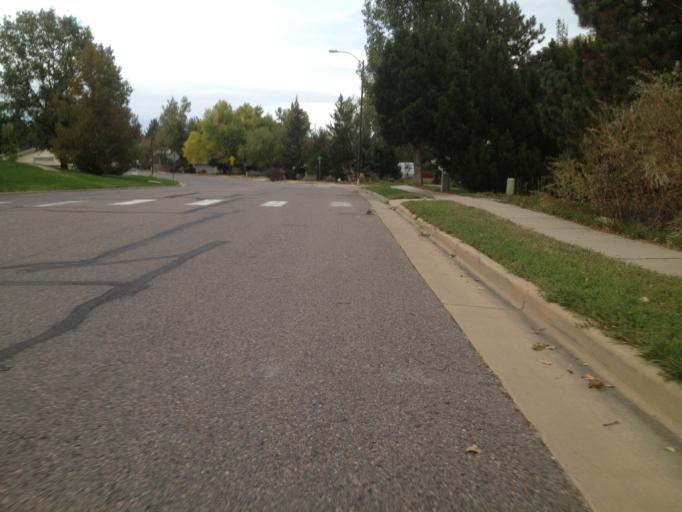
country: US
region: Colorado
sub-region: Boulder County
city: Louisville
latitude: 39.9878
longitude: -105.1380
